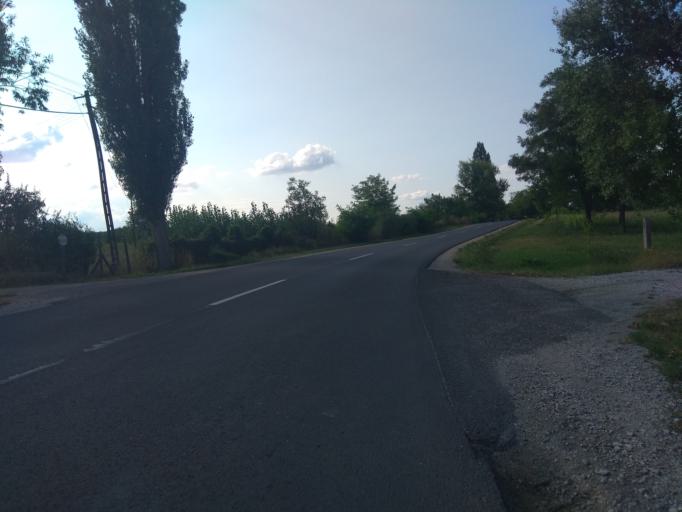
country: HU
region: Borsod-Abauj-Zemplen
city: Mezocsat
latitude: 47.8394
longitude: 20.8988
